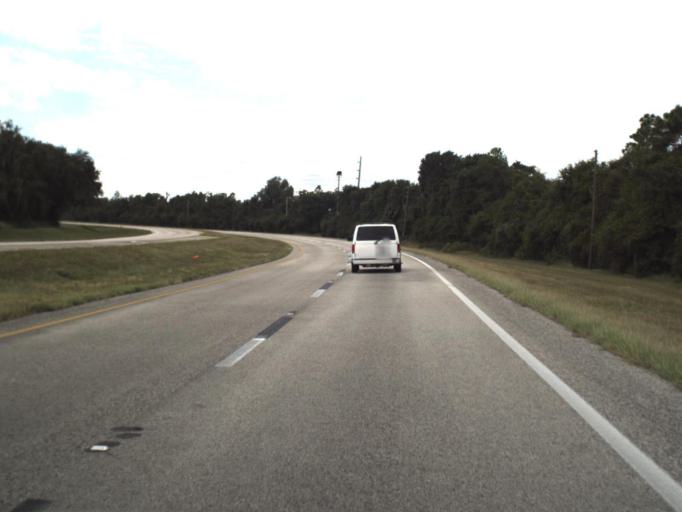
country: US
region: Florida
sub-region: Hardee County
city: Bowling Green
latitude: 27.6800
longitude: -81.8197
